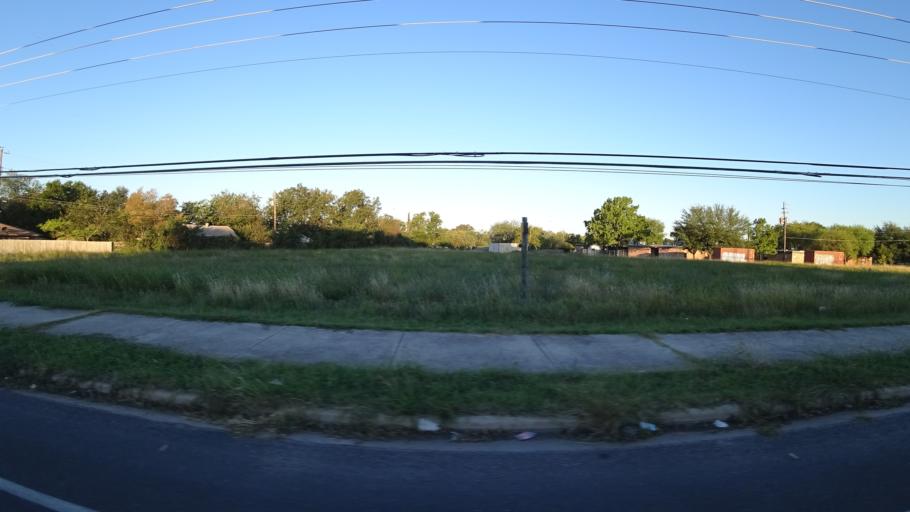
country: US
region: Texas
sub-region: Travis County
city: Austin
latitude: 30.2997
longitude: -97.6739
